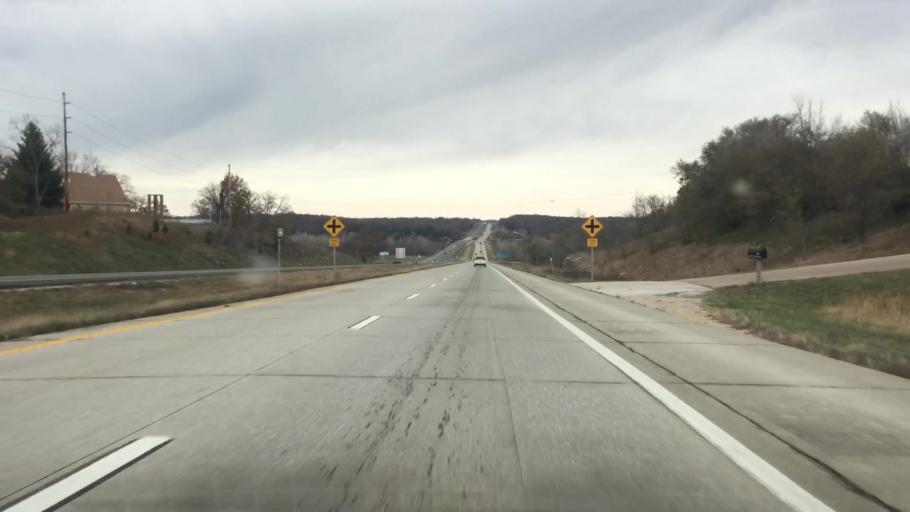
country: US
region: Missouri
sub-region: Saint Clair County
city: Osceola
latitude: 38.0493
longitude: -93.6863
